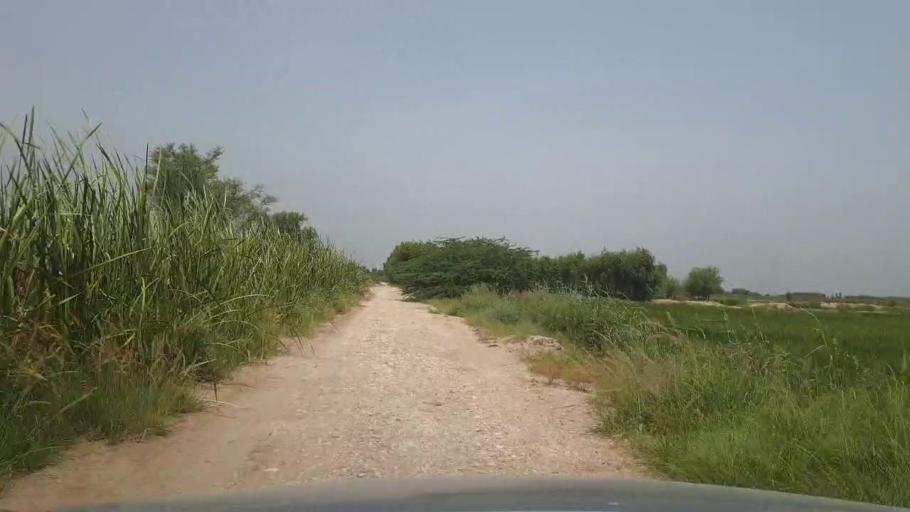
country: PK
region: Sindh
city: Garhi Yasin
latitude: 27.9443
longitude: 68.4298
